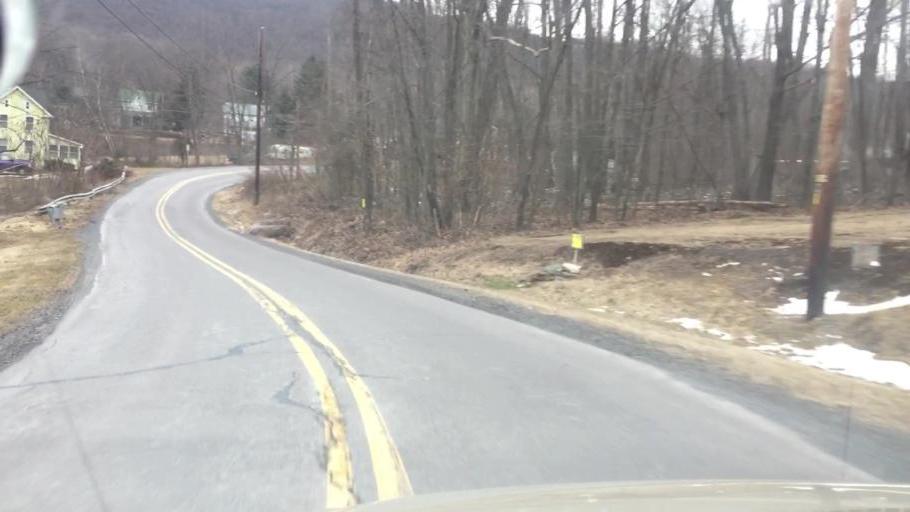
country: US
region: Pennsylvania
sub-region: Luzerne County
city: Oakdale
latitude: 41.0125
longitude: -75.9503
